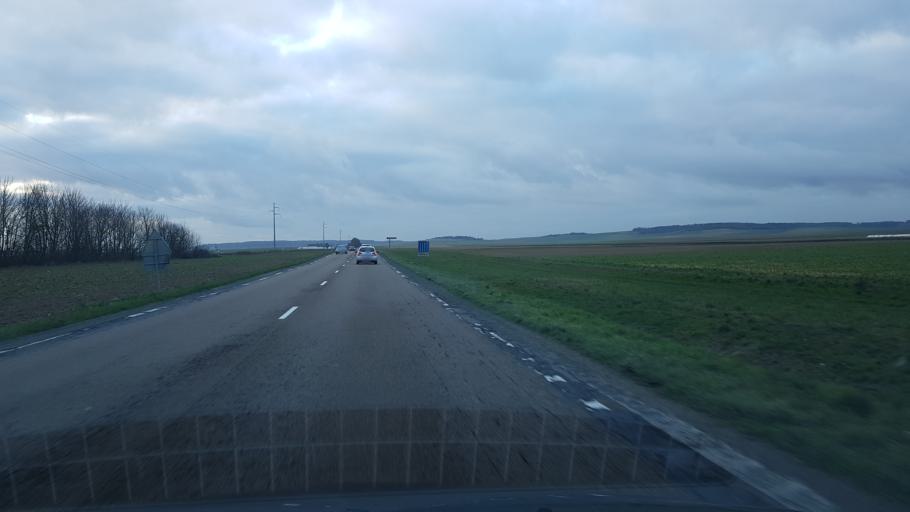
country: FR
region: Champagne-Ardenne
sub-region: Departement de la Marne
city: Sezanne
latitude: 48.7231
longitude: 3.8086
